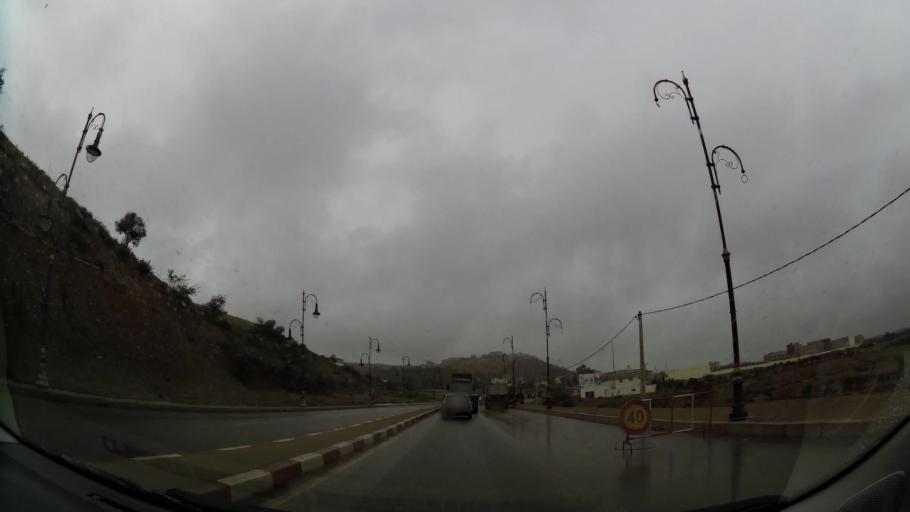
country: MA
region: Taza-Al Hoceima-Taounate
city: Imzourene
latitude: 35.1595
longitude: -3.8533
